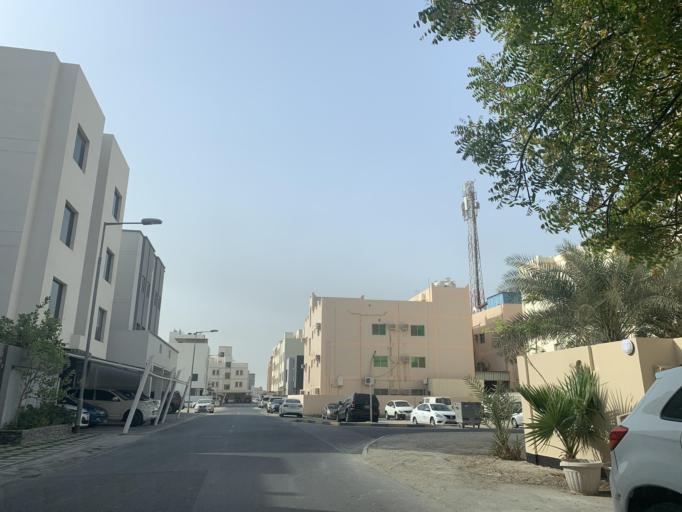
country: BH
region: Northern
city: Madinat `Isa
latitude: 26.1891
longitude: 50.5622
